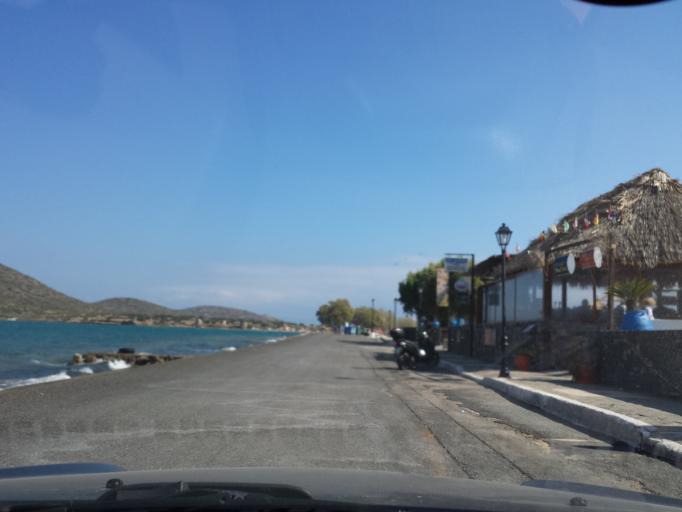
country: GR
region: Crete
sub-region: Nomos Lasithiou
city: Skhisma
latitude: 35.2585
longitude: 25.7293
